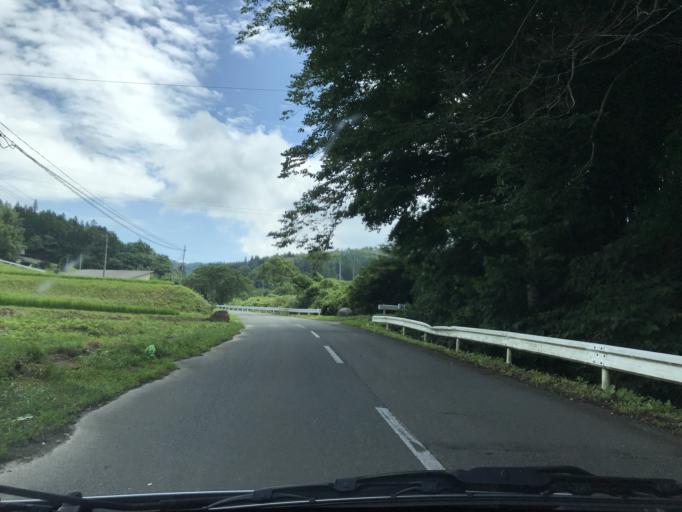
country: JP
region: Iwate
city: Mizusawa
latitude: 39.0592
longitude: 141.3967
